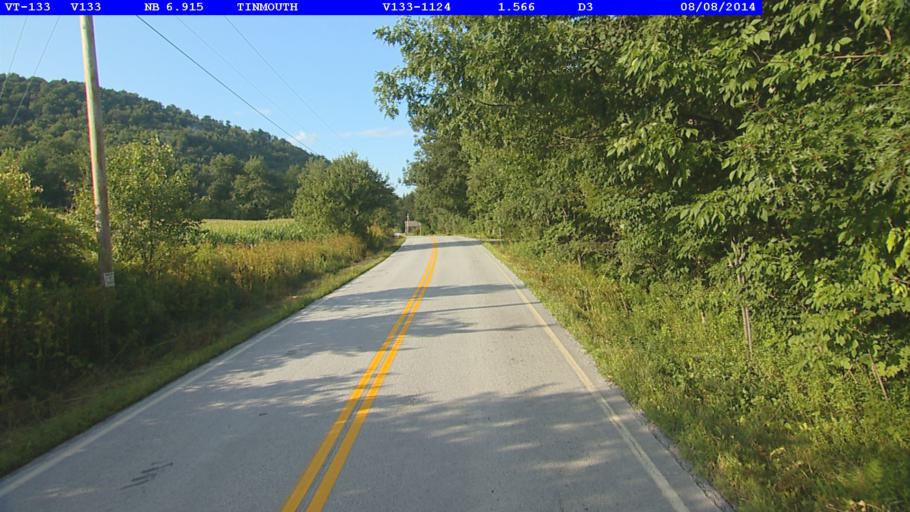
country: US
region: New York
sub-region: Washington County
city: Granville
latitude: 43.4248
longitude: -73.1172
